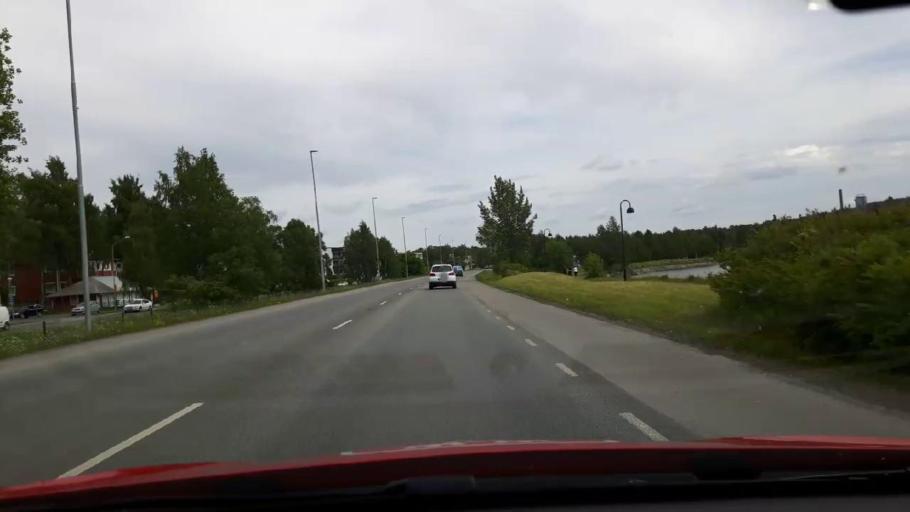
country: SE
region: Jaemtland
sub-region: Krokoms Kommun
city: Krokom
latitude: 63.1144
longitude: 14.4337
